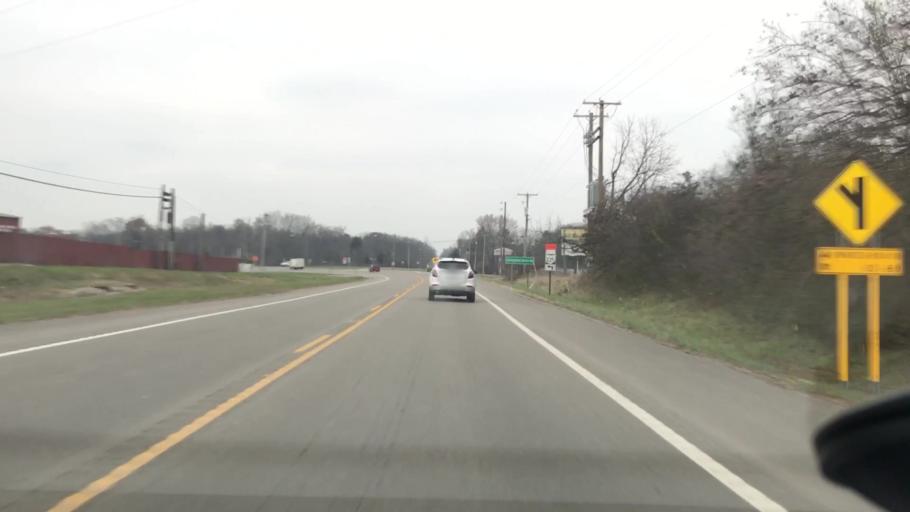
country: US
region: Ohio
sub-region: Clark County
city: Springfield
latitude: 39.8717
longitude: -83.8449
